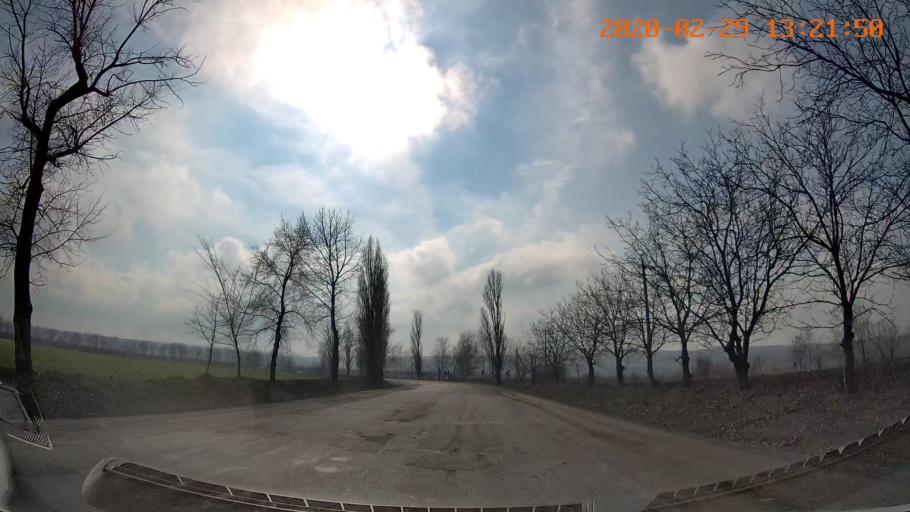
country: MD
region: Telenesti
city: Camenca
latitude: 47.9668
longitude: 28.6295
